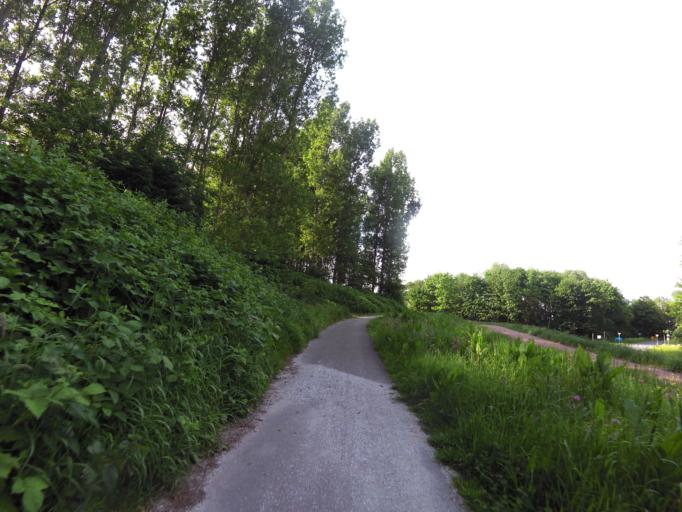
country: NL
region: South Holland
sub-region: Gemeente Pijnacker-Nootdorp
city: Pijnacker
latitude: 52.0564
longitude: 4.4378
